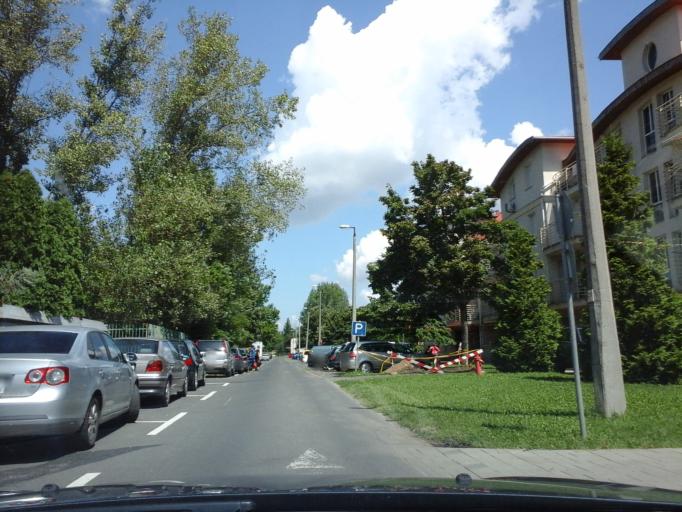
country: HU
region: Hajdu-Bihar
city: Hajduszoboszlo
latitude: 47.4521
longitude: 21.4060
